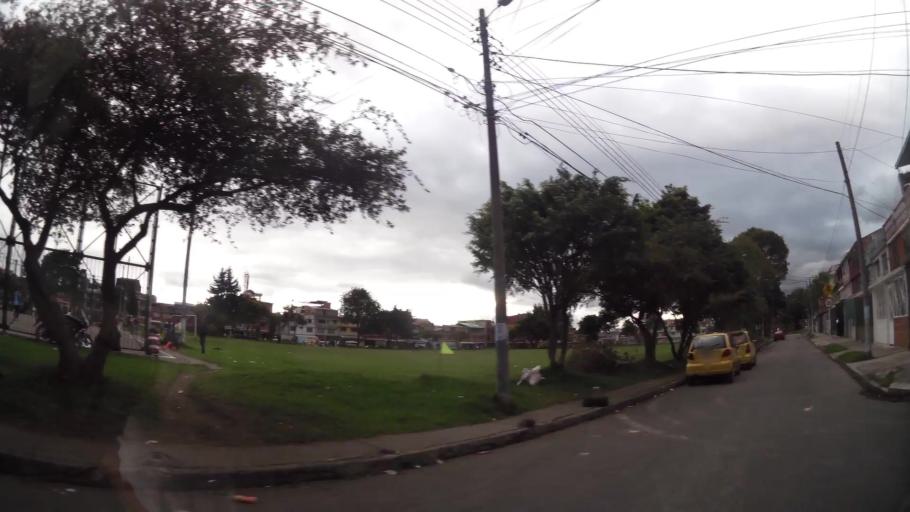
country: CO
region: Bogota D.C.
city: Bogota
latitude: 4.6889
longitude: -74.1056
